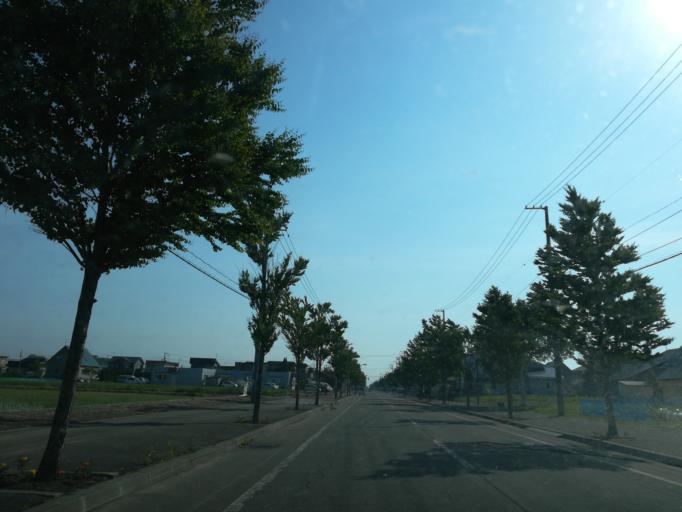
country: JP
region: Hokkaido
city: Ebetsu
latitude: 43.1462
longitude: 141.6577
